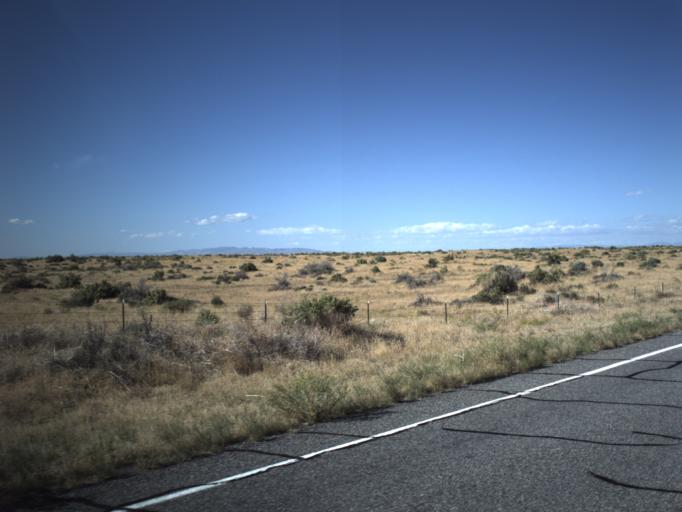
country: US
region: Utah
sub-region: Millard County
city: Delta
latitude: 39.3535
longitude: -112.4656
